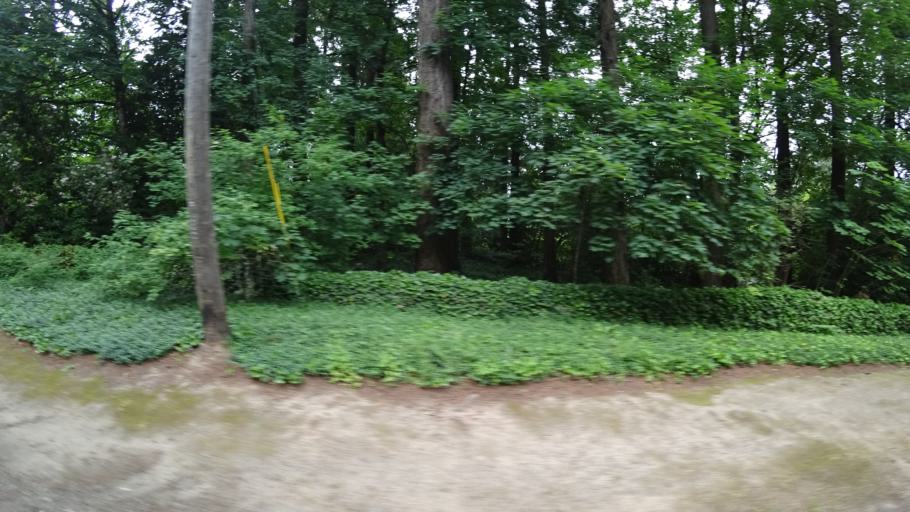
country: US
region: Oregon
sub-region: Clackamas County
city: Lake Oswego
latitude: 45.4320
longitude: -122.6599
